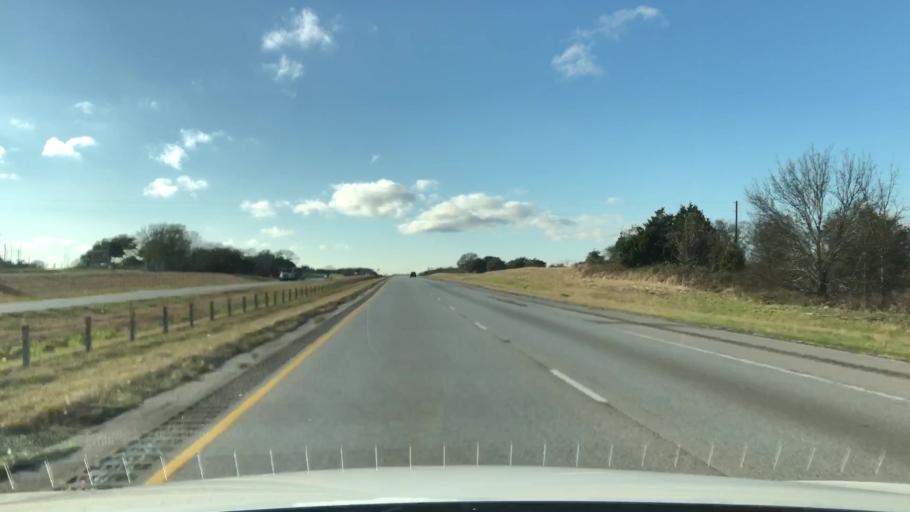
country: US
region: Texas
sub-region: Colorado County
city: Weimar
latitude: 29.6892
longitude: -96.7083
